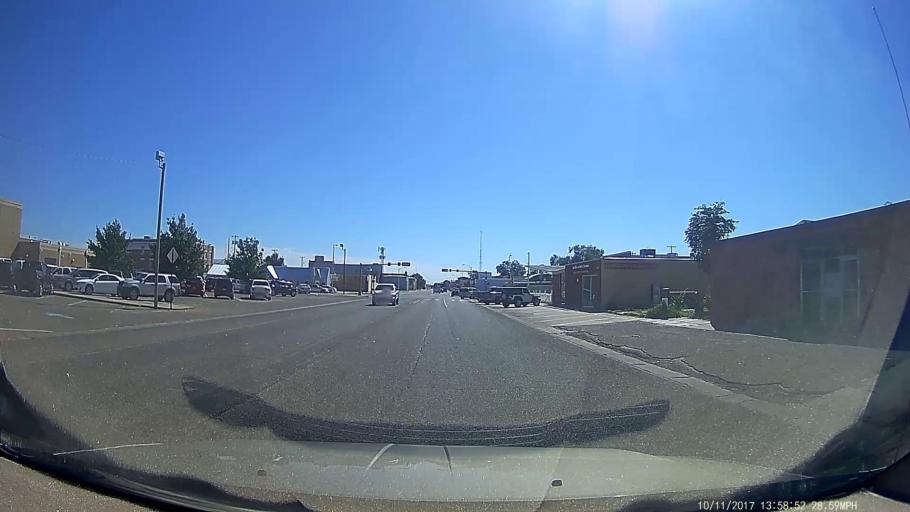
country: US
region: New Mexico
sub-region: Curry County
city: Clovis
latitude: 34.4056
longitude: -103.2067
